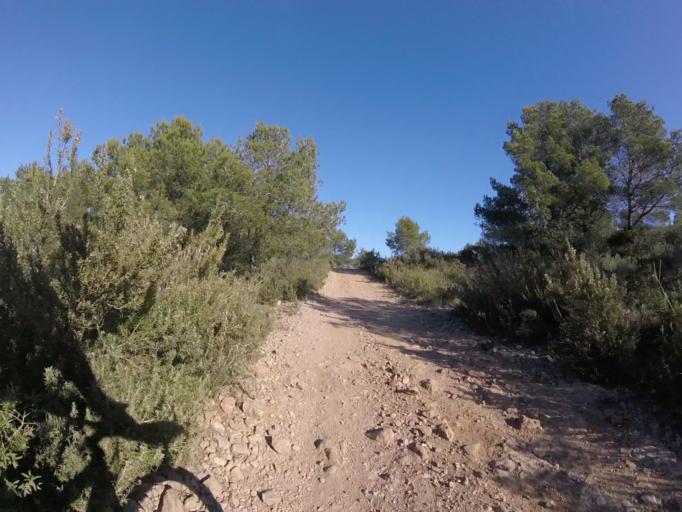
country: ES
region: Valencia
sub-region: Provincia de Castello
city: Orpesa/Oropesa del Mar
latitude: 40.0908
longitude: 0.1038
